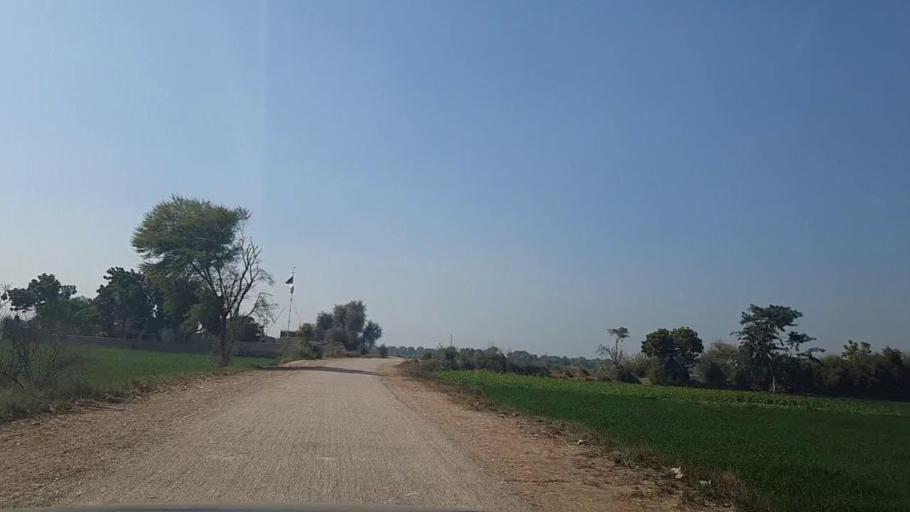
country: PK
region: Sindh
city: Daulatpur
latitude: 26.2846
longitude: 68.0477
